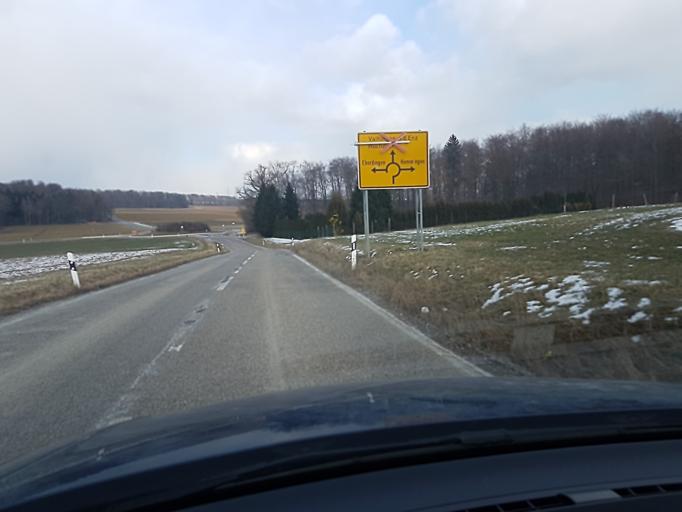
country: DE
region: Baden-Wuerttemberg
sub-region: Regierungsbezirk Stuttgart
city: Eberdingen
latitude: 48.8627
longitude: 8.9878
